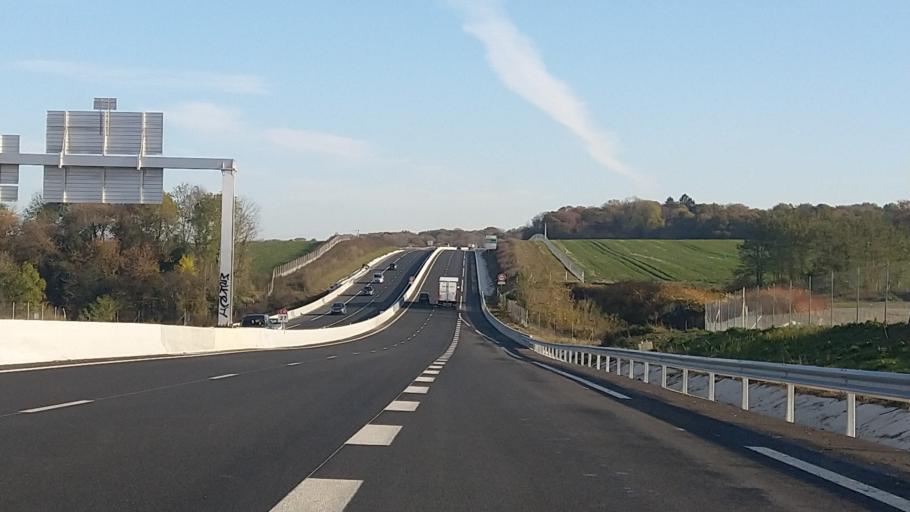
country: FR
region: Ile-de-France
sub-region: Departement du Val-d'Oise
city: Mours
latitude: 49.1003
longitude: 2.2800
